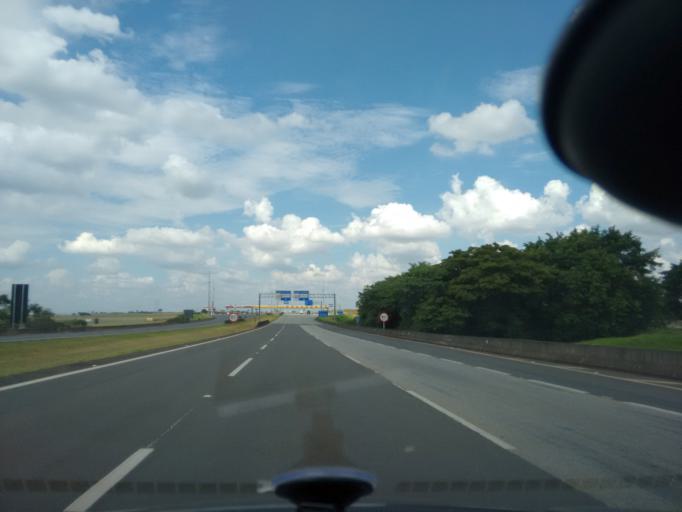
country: BR
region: Sao Paulo
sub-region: Sumare
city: Sumare
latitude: -22.8566
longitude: -47.3058
